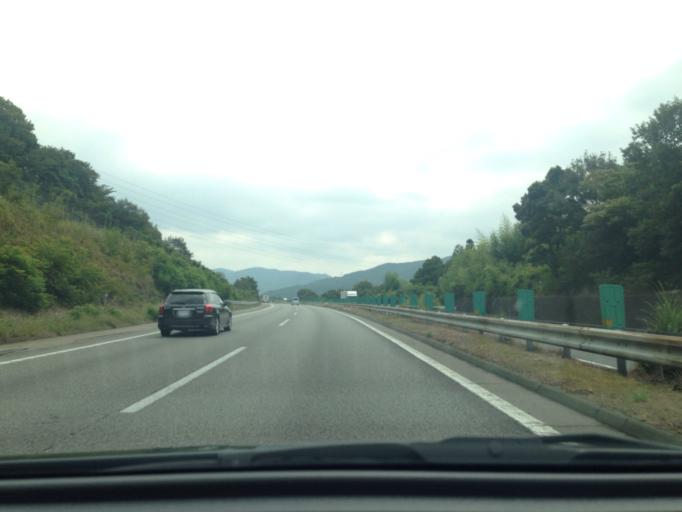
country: JP
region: Aichi
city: Shinshiro
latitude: 34.8444
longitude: 137.4785
